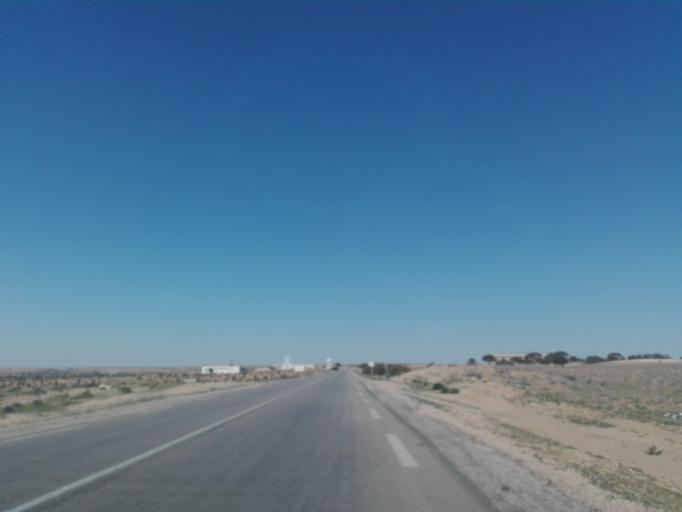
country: TN
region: Safaqis
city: Bi'r `Ali Bin Khalifah
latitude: 34.7386
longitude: 10.4049
